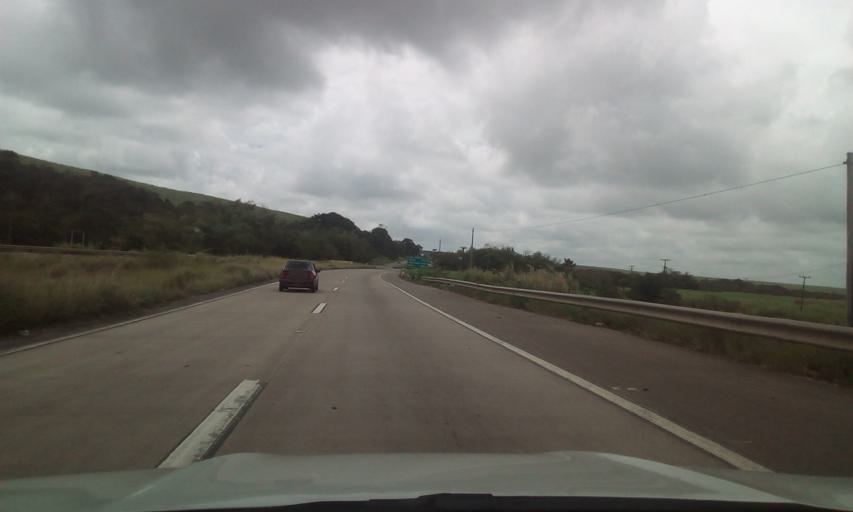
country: BR
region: Pernambuco
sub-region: Itapissuma
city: Itapissuma
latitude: -7.7594
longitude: -34.9355
